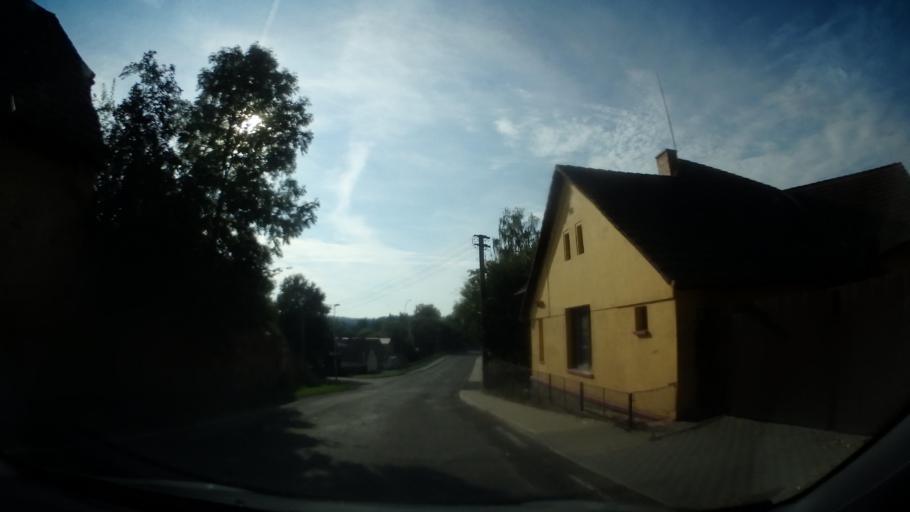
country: CZ
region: Jihocesky
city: Cimelice
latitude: 49.4205
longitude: 14.1157
